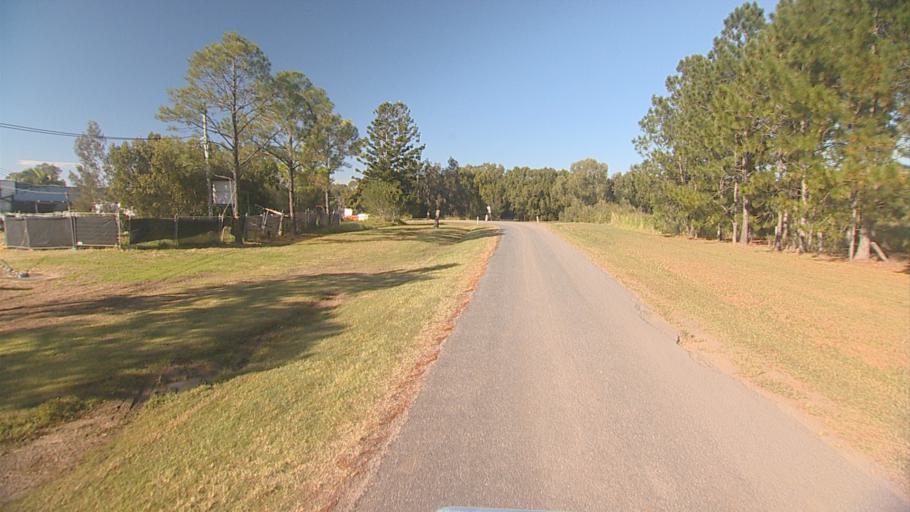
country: AU
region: Queensland
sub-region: Gold Coast
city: Yatala
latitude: -27.6906
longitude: 153.2606
